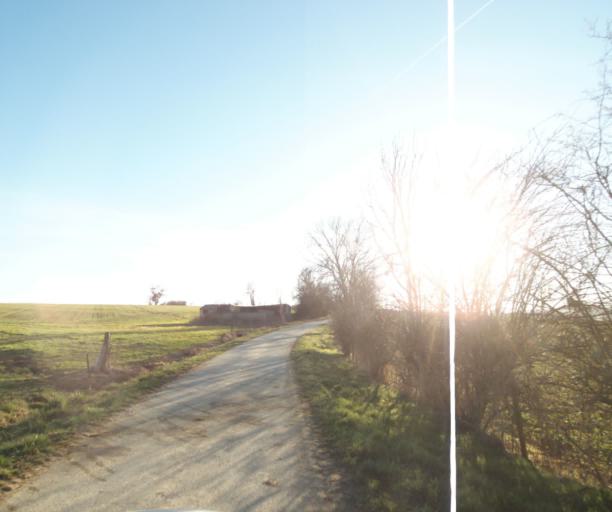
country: FR
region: Lorraine
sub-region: Departement de Meurthe-et-Moselle
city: Laneuveville-devant-Nancy
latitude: 48.6416
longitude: 6.2326
